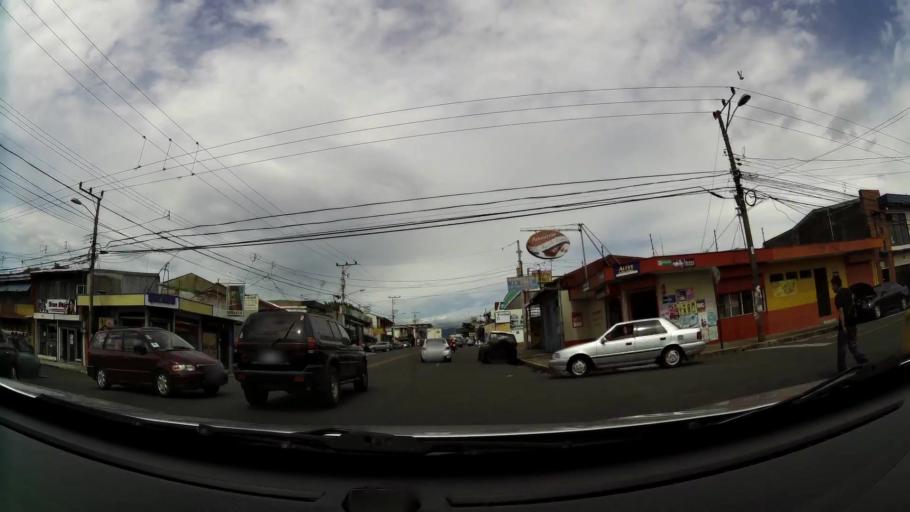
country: CR
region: San Jose
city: San Jose
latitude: 9.9217
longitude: -84.0751
